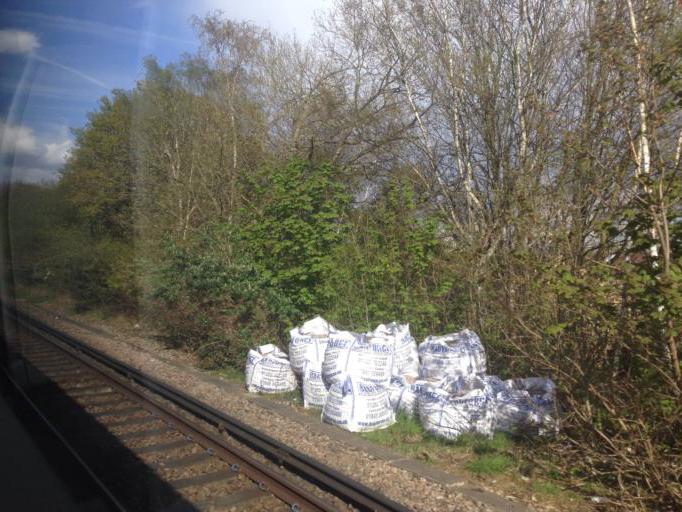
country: GB
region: England
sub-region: Greater London
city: Mitcham
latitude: 51.4176
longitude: -0.1427
